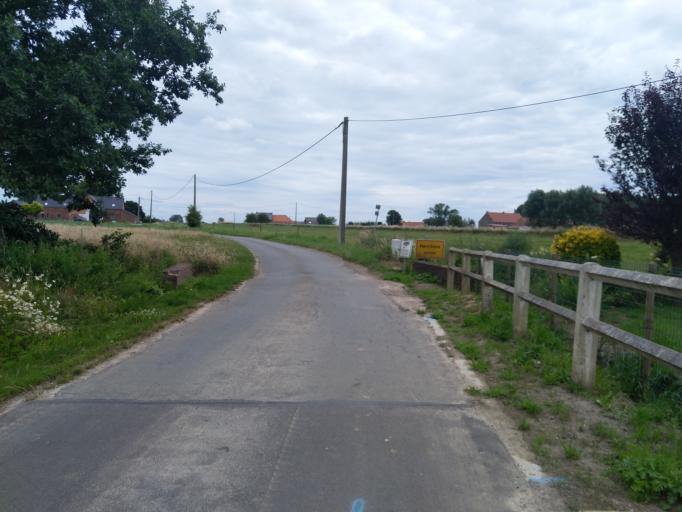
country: BE
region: Wallonia
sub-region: Province du Hainaut
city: Chievres
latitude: 50.5426
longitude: 3.8114
